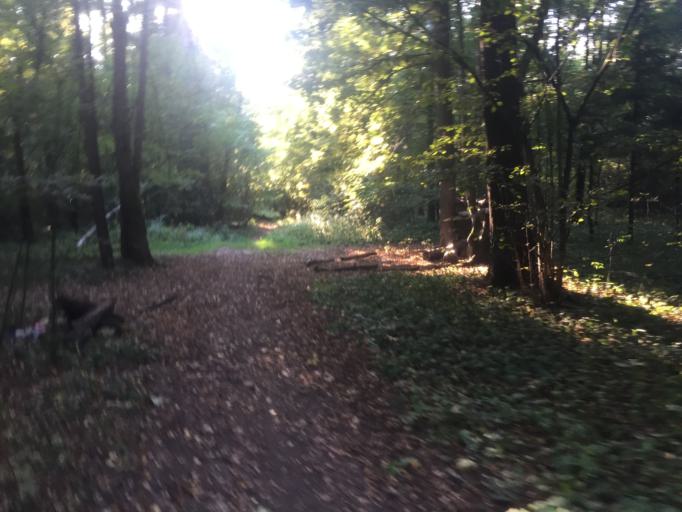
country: RU
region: Moscow
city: Gol'yanovo
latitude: 55.8397
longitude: 37.7977
